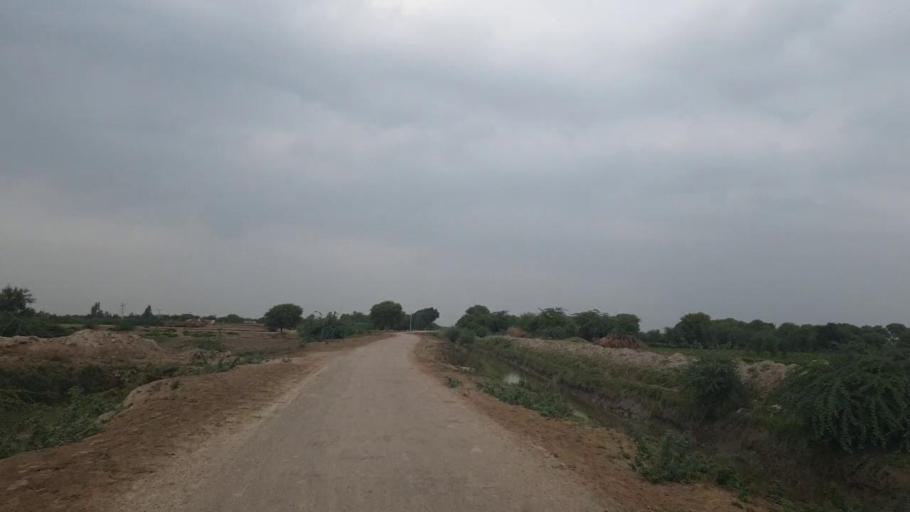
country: PK
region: Sindh
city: Badin
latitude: 24.6297
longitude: 68.6817
